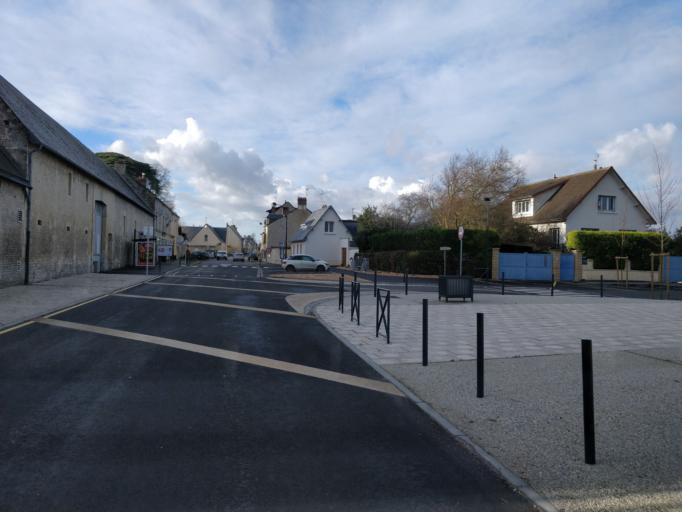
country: FR
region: Lower Normandy
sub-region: Departement du Calvados
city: Saint-Manvieu
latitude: 49.2114
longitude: -0.5151
